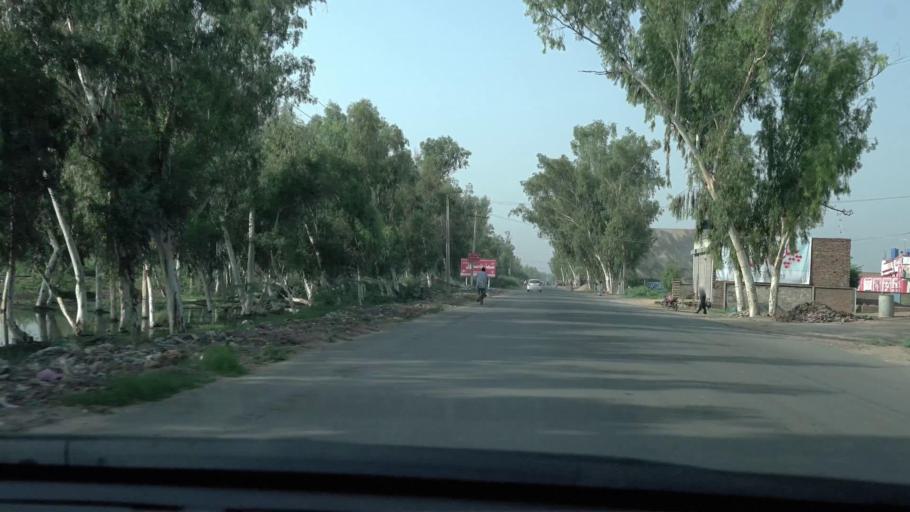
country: PK
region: Punjab
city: Gojra
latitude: 31.1186
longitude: 72.6682
